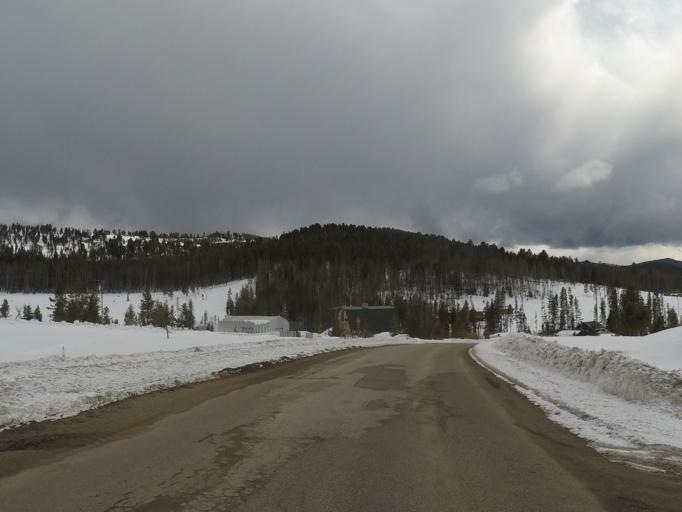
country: US
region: Montana
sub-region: Granite County
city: Philipsburg
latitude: 46.1997
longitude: -113.2527
